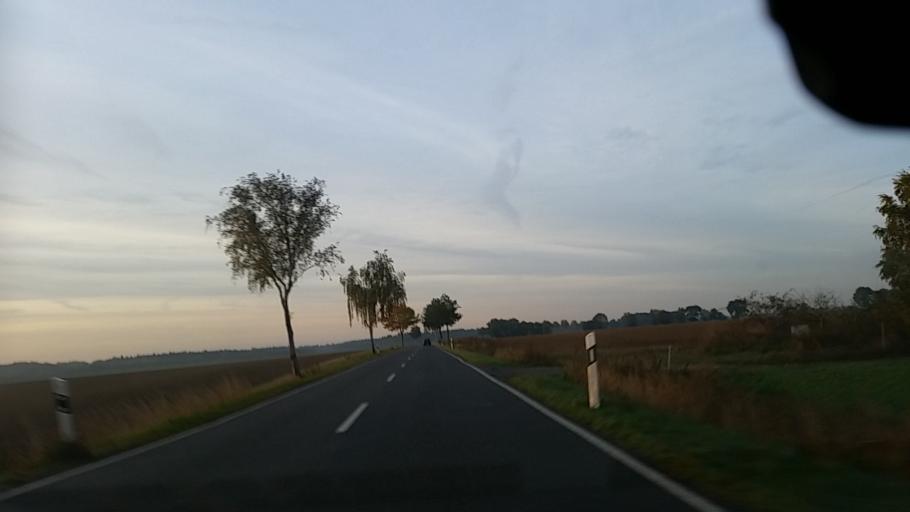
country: DE
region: Lower Saxony
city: Wittingen
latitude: 52.6875
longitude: 10.8071
